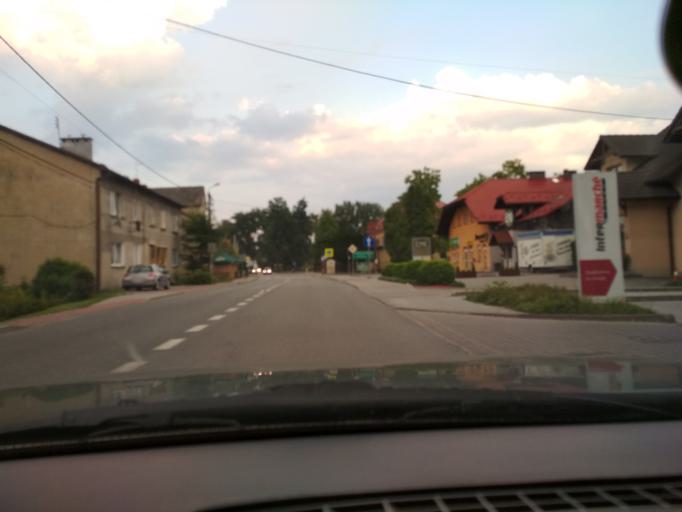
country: PL
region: Silesian Voivodeship
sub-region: Powiat cieszynski
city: Mnich
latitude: 49.8926
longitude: 18.8177
